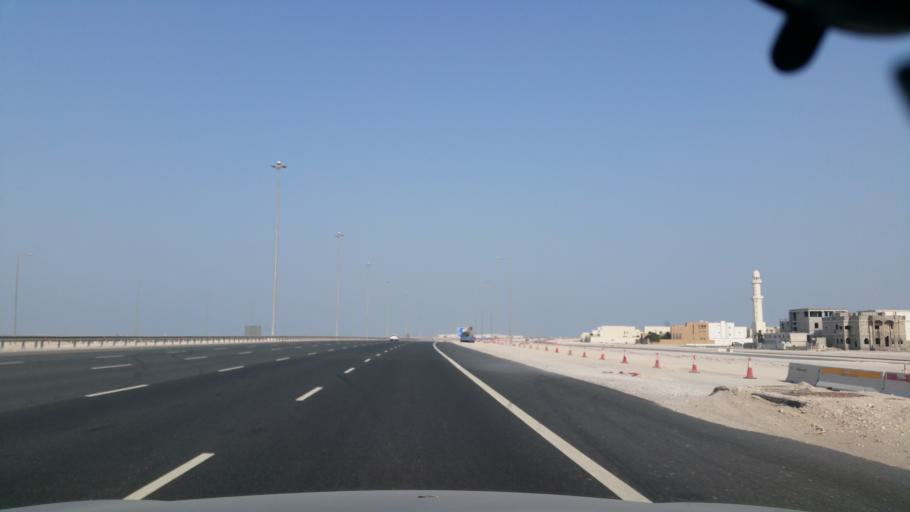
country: QA
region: Baladiyat Umm Salal
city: Umm Salal `Ali
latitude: 25.4554
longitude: 51.4375
